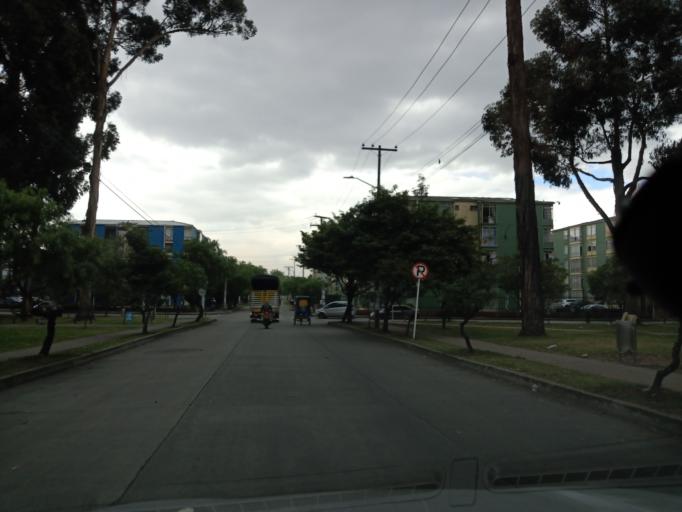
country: CO
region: Bogota D.C.
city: Bogota
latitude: 4.5730
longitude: -74.1060
